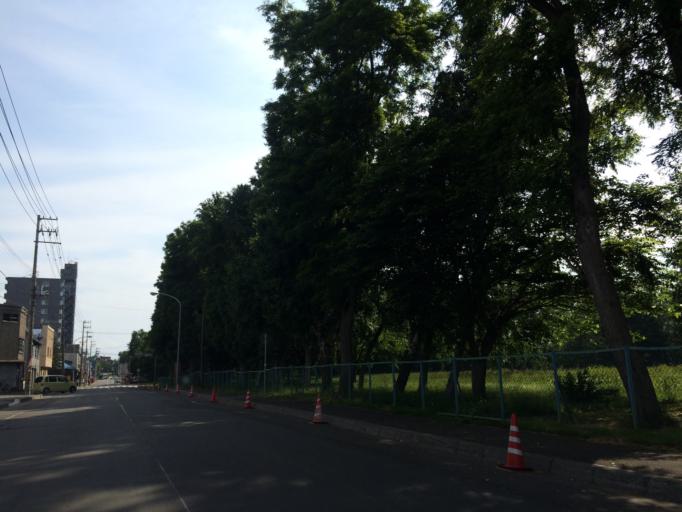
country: JP
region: Hokkaido
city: Ebetsu
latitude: 43.1150
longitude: 141.5564
